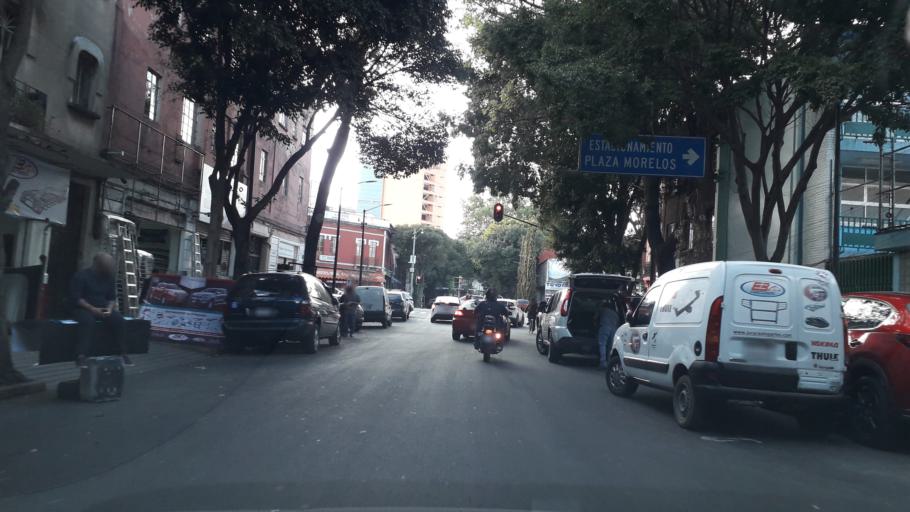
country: MX
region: Mexico City
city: Cuauhtemoc
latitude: 19.4278
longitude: -99.1538
